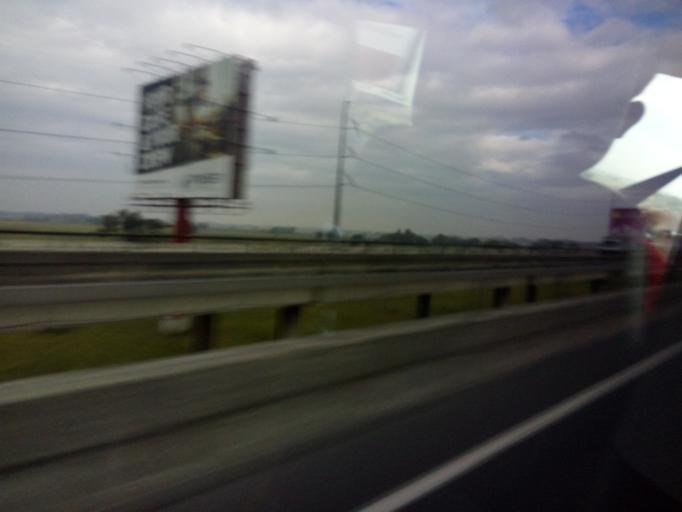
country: PH
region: Central Luzon
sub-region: Province of Pampanga
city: Balucuc
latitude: 14.9300
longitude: 120.7981
